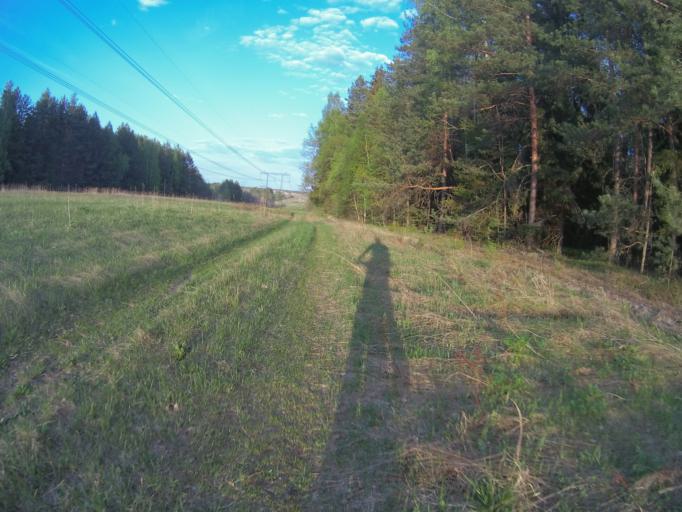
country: RU
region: Vladimir
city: Kommunar
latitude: 56.0566
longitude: 40.4669
